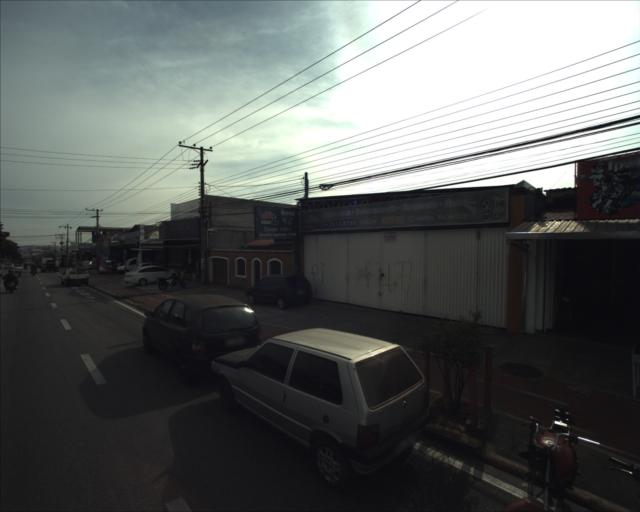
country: BR
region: Sao Paulo
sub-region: Sorocaba
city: Sorocaba
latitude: -23.4754
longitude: -47.4866
